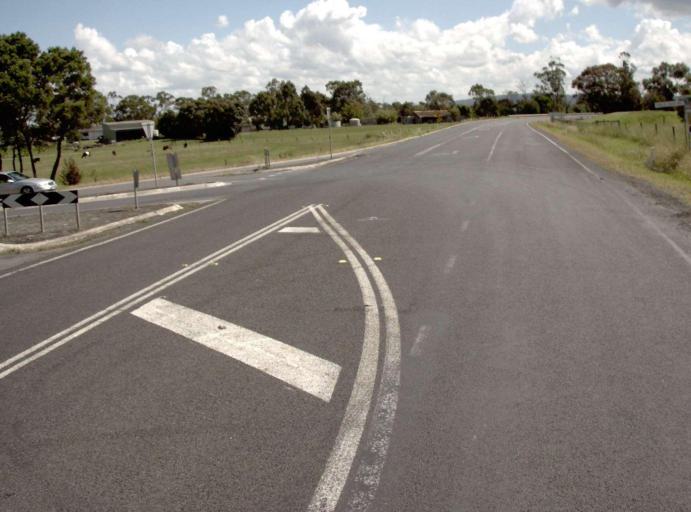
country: AU
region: Victoria
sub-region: Latrobe
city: Morwell
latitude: -38.1611
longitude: 146.4069
